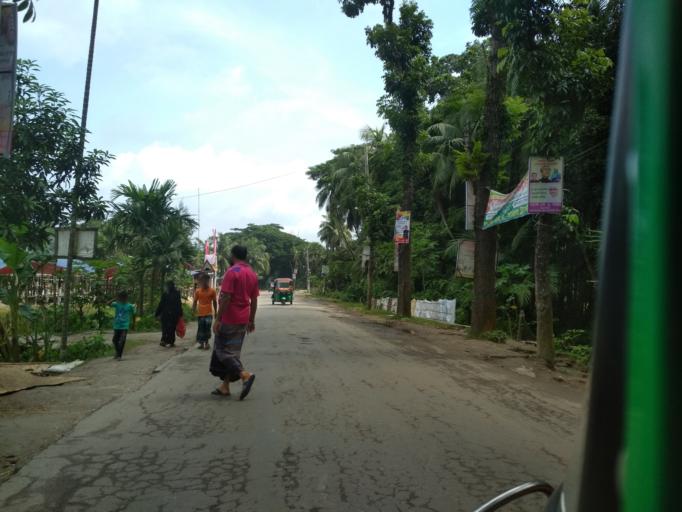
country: BD
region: Chittagong
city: Lakshmipur
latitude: 22.9484
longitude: 90.8086
